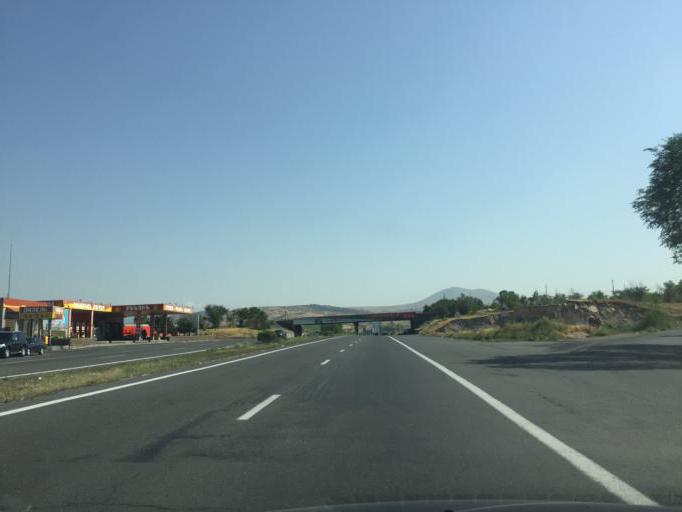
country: AM
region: Kotayk'i Marz
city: Arzni
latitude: 40.2833
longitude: 44.6051
